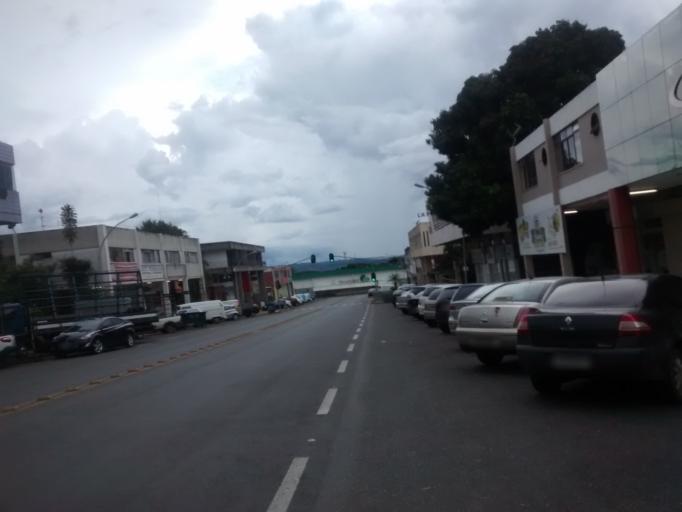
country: BR
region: Federal District
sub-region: Brasilia
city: Brasilia
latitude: -15.7734
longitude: -47.8771
